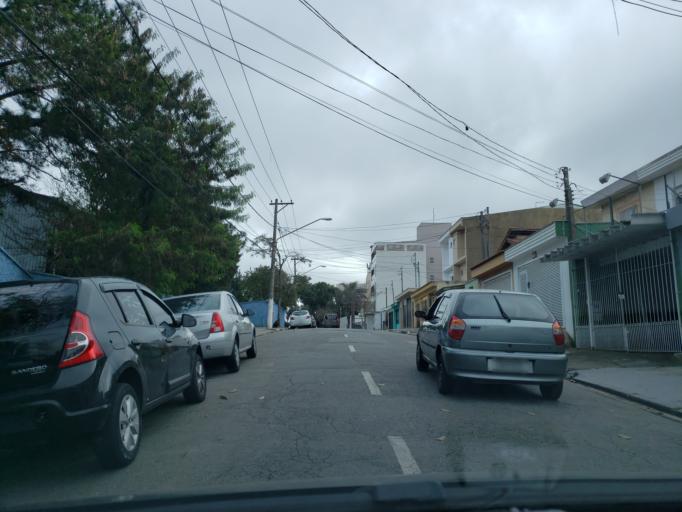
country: BR
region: Sao Paulo
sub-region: Sao Bernardo Do Campo
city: Sao Bernardo do Campo
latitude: -23.6743
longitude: -46.5618
